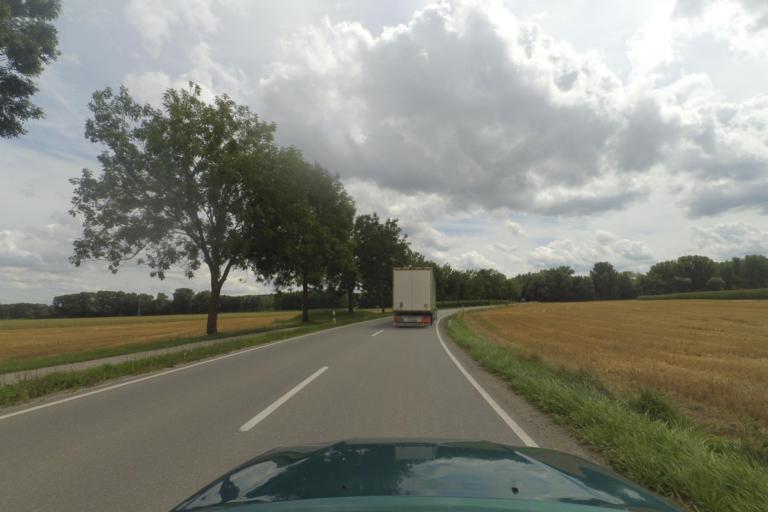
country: DE
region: Bavaria
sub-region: Lower Bavaria
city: Mamming
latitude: 48.6623
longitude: 12.5982
